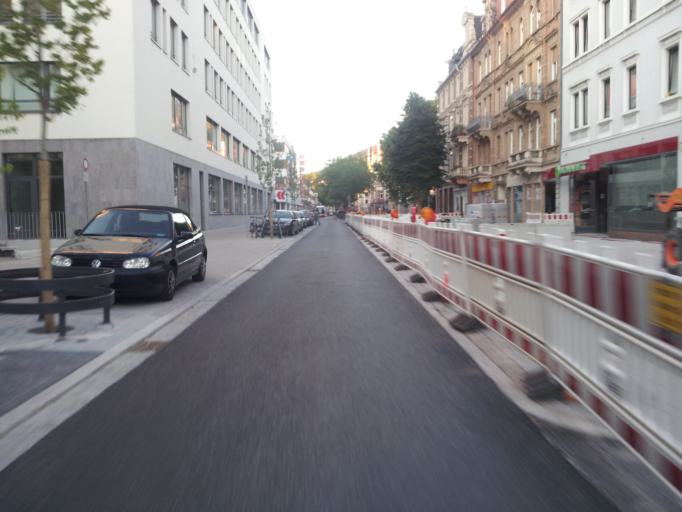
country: DE
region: Baden-Wuerttemberg
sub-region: Karlsruhe Region
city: Heidelberg
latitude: 49.4057
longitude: 8.6880
